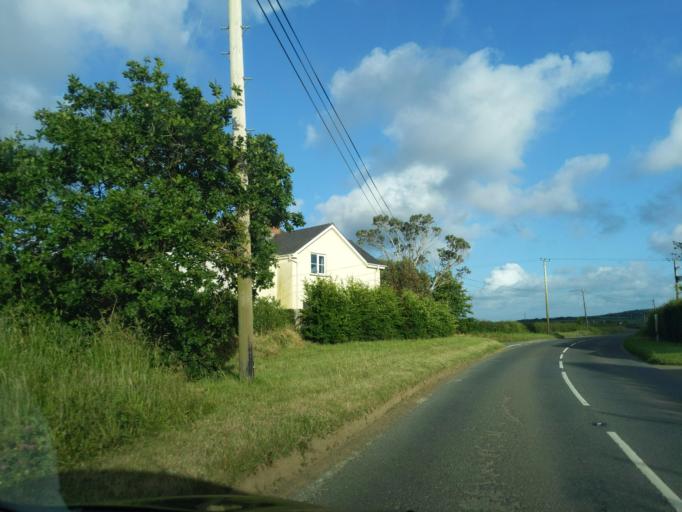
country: GB
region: England
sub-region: Devon
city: Fremington
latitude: 51.0034
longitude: -4.1031
